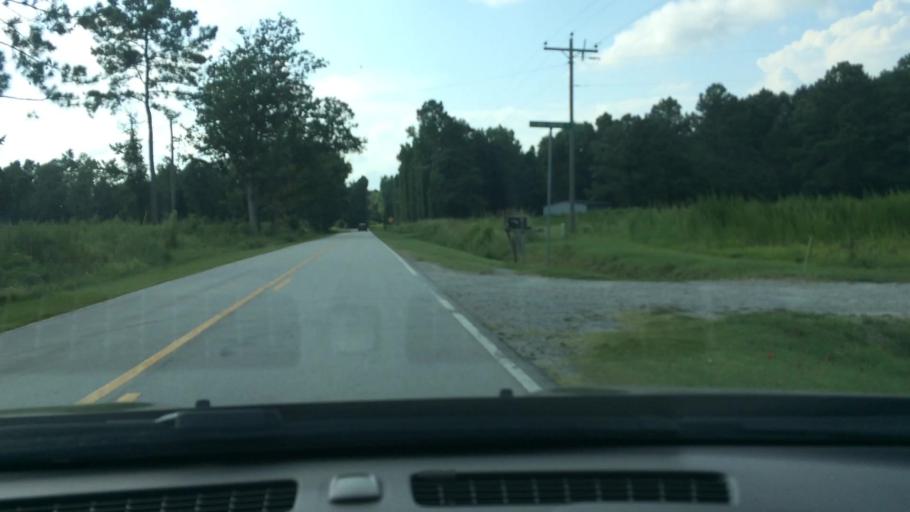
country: US
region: North Carolina
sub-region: Beaufort County
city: River Road
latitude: 35.4330
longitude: -76.9823
